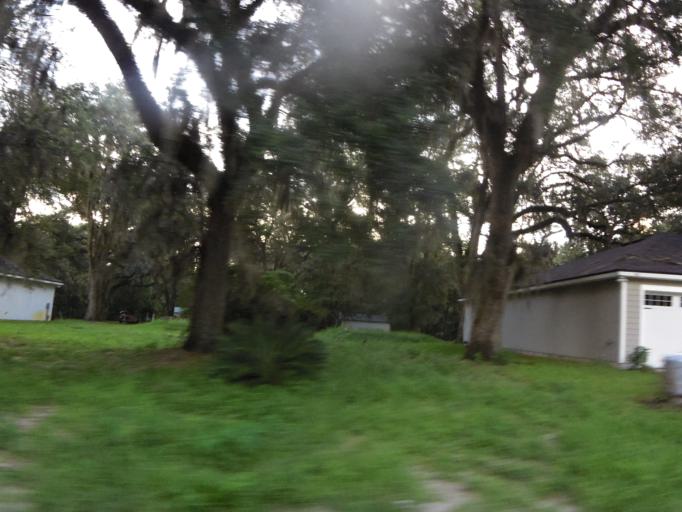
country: US
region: Florida
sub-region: Duval County
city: Jacksonville
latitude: 30.3336
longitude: -81.7839
